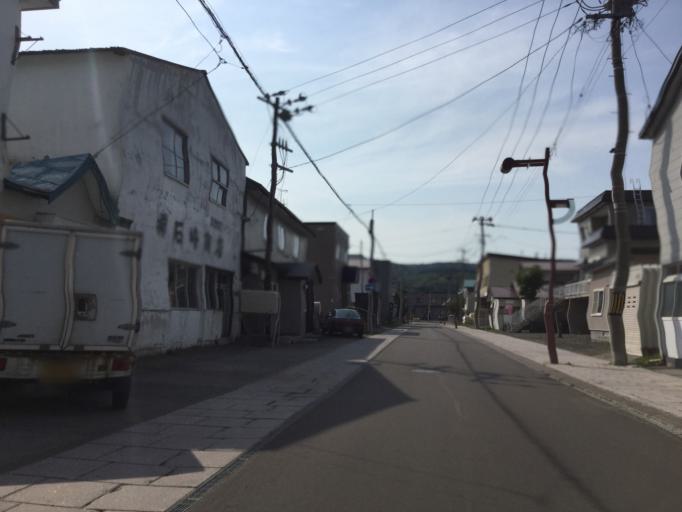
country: JP
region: Hokkaido
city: Wakkanai
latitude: 45.3988
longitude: 141.6825
